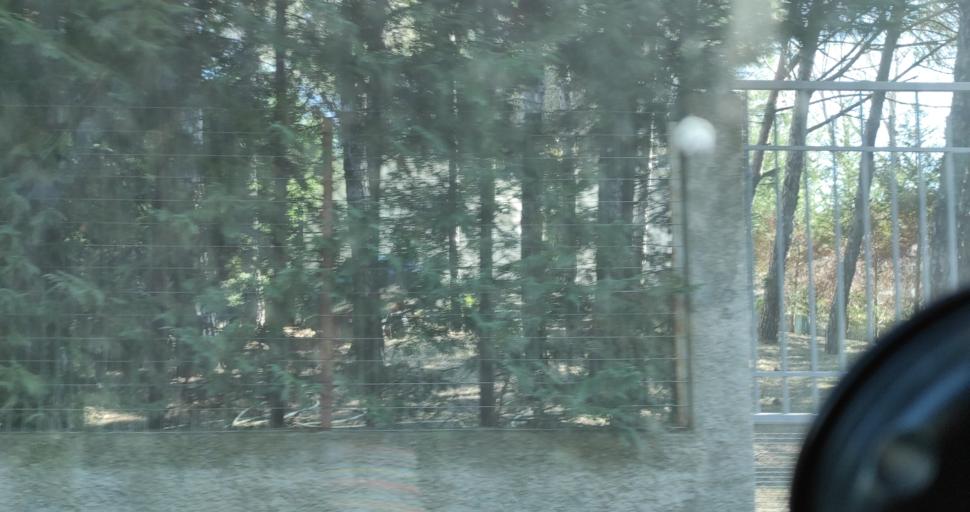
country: AL
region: Shkoder
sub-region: Rrethi i Shkodres
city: Velipoje
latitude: 41.8640
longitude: 19.4171
